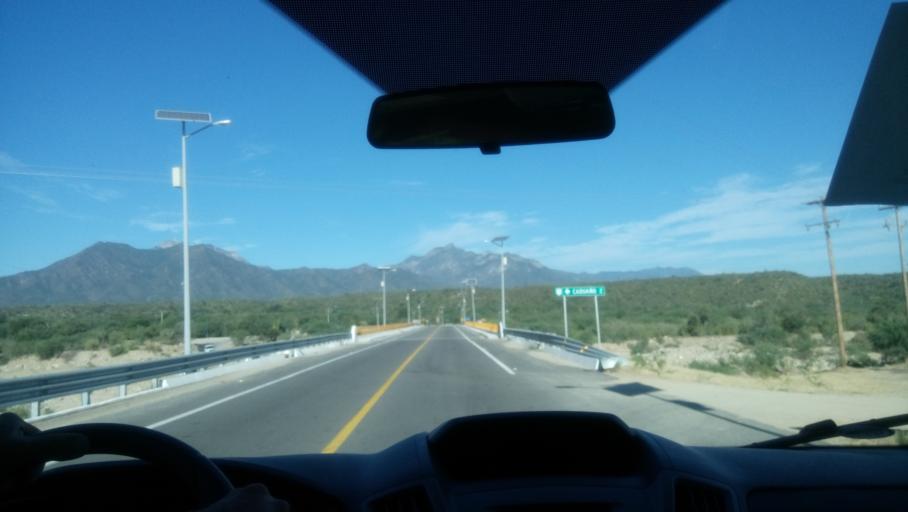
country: MX
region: Baja California Sur
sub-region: Los Cabos
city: Las Veredas
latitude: 23.3313
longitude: -109.7652
